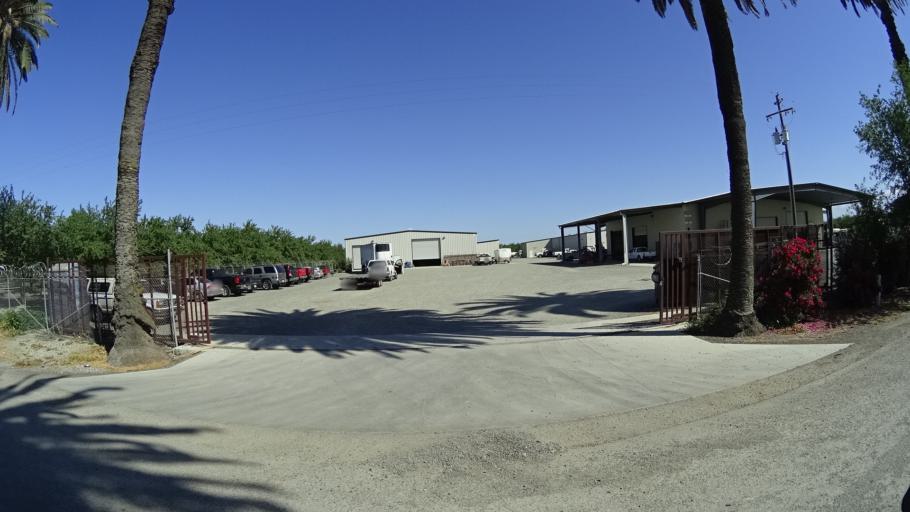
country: US
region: California
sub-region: Glenn County
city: Hamilton City
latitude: 39.7374
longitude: -122.0514
